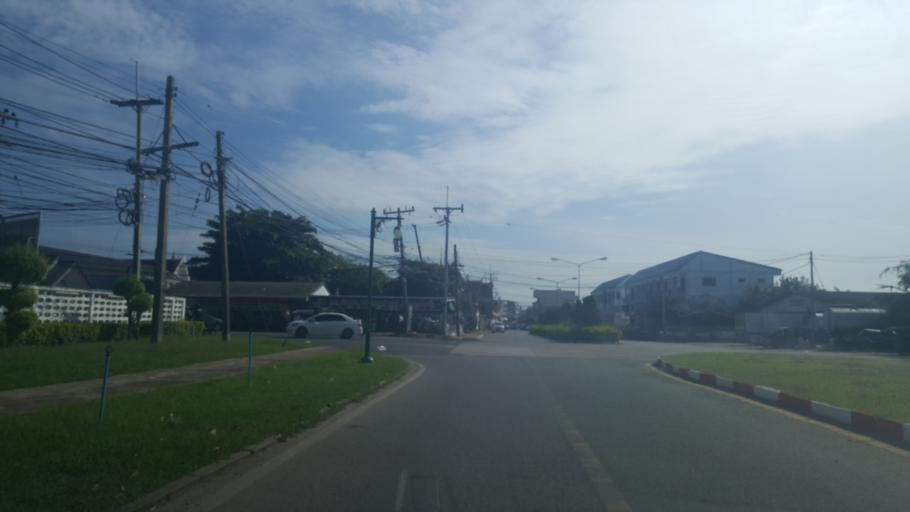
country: TH
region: Chon Buri
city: Sattahip
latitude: 12.6620
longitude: 100.8968
